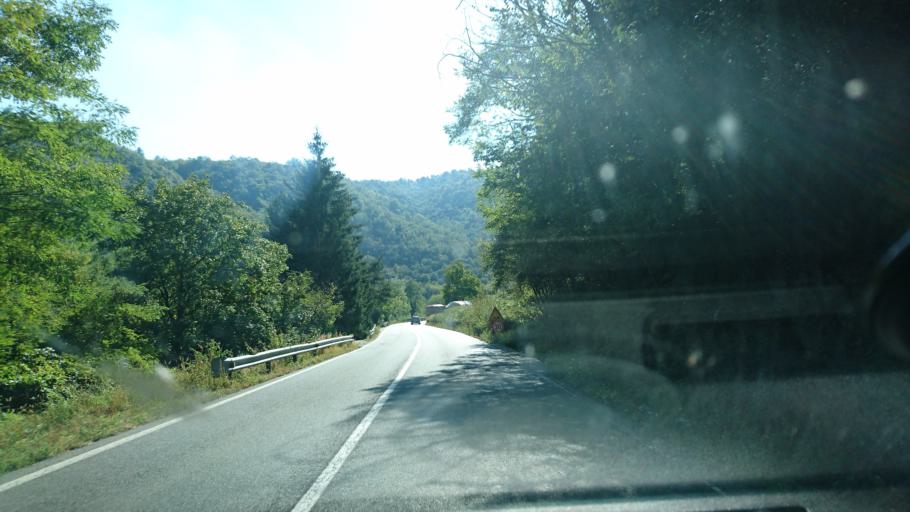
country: IT
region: Piedmont
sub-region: Provincia di Alessandria
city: Spigno Monferrato
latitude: 44.5341
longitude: 8.3259
